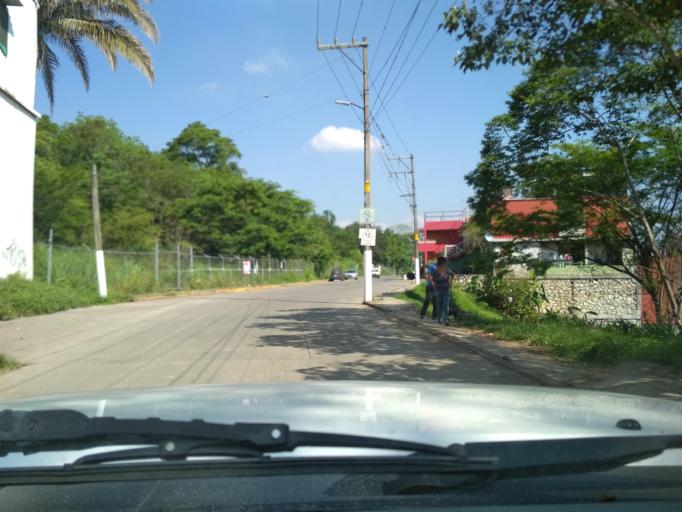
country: MX
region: Veracruz
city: Amatlan de los Reyes
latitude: 18.8705
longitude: -96.9071
